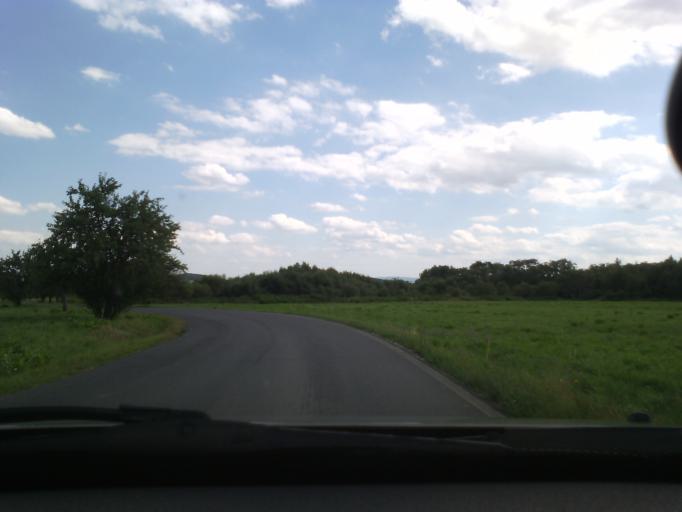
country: SK
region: Presovsky
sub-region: Okres Poprad
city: Nova Lesna
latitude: 49.1308
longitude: 20.3197
